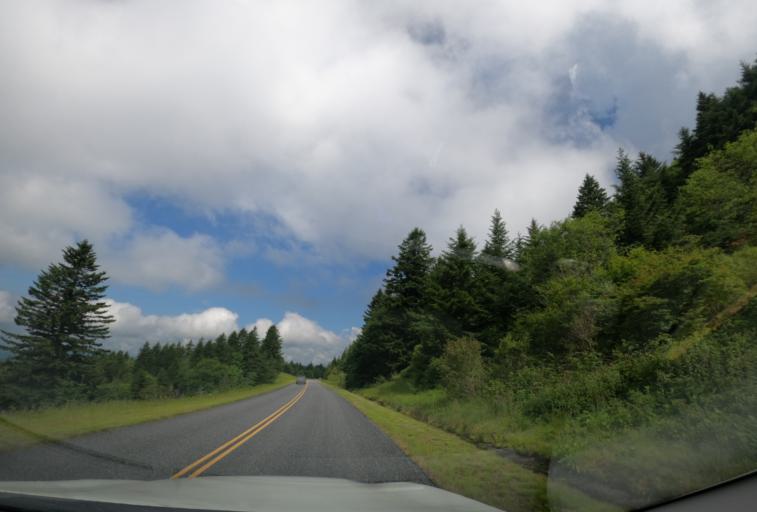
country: US
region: North Carolina
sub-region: Haywood County
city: Hazelwood
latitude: 35.3658
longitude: -82.9932
